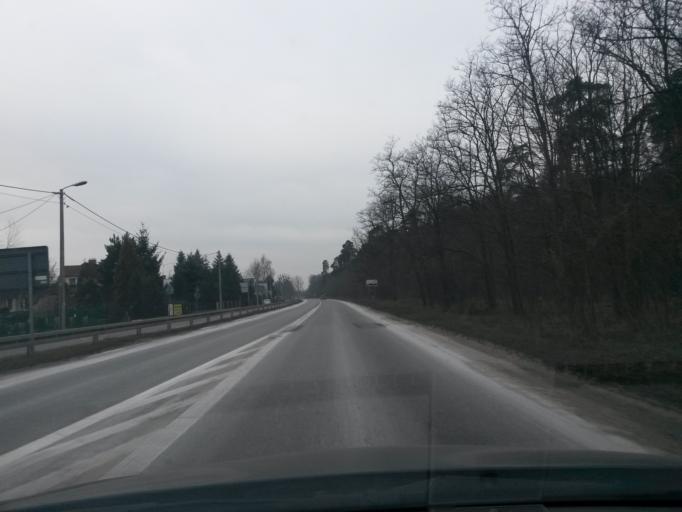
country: PL
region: Greater Poland Voivodeship
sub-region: Powiat poznanski
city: Kobylnica
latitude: 52.4458
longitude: 17.0749
